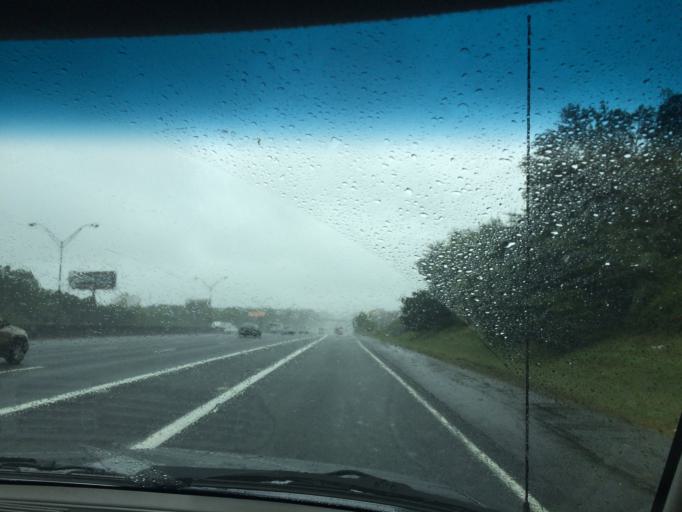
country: US
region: Georgia
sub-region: Cobb County
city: Marietta
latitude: 33.9653
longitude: -84.5230
